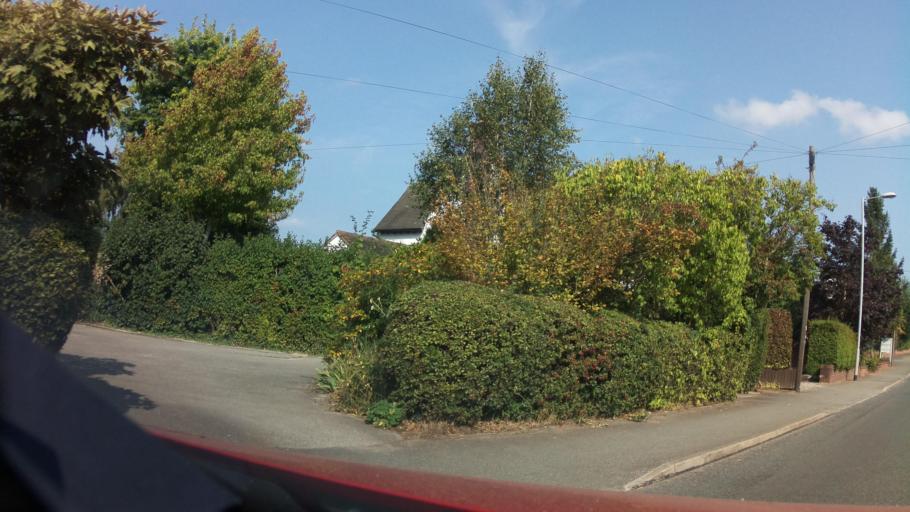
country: GB
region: England
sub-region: Staffordshire
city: Lichfield
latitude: 52.6724
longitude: -1.8320
